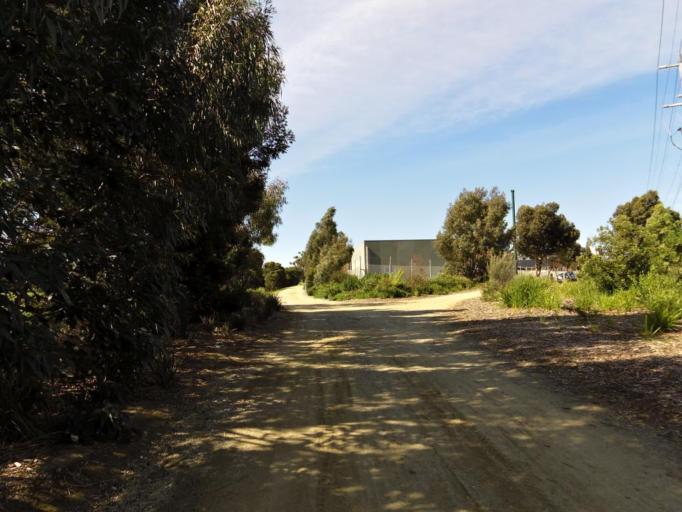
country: AU
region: Victoria
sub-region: Greater Dandenong
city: Dandenong
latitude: -37.9974
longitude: 145.1970
